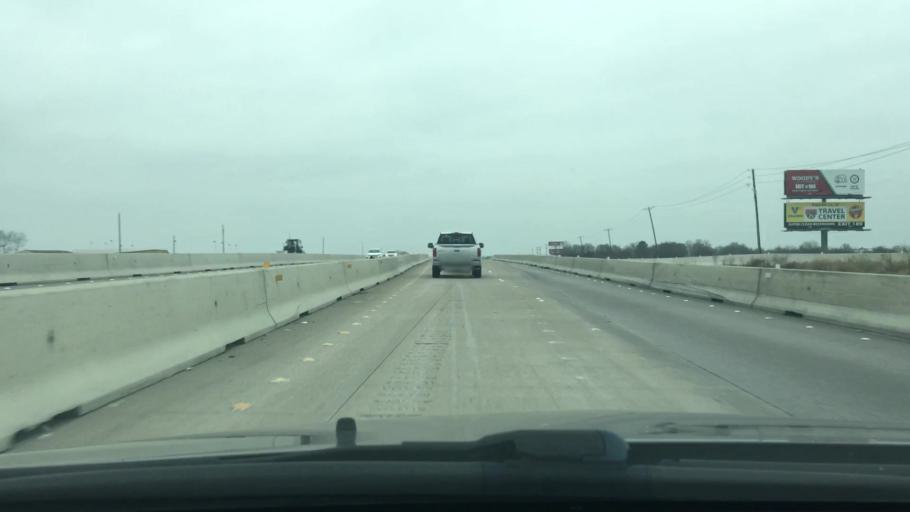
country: US
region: Texas
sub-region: Navarro County
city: Corsicana
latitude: 32.0362
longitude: -96.4452
